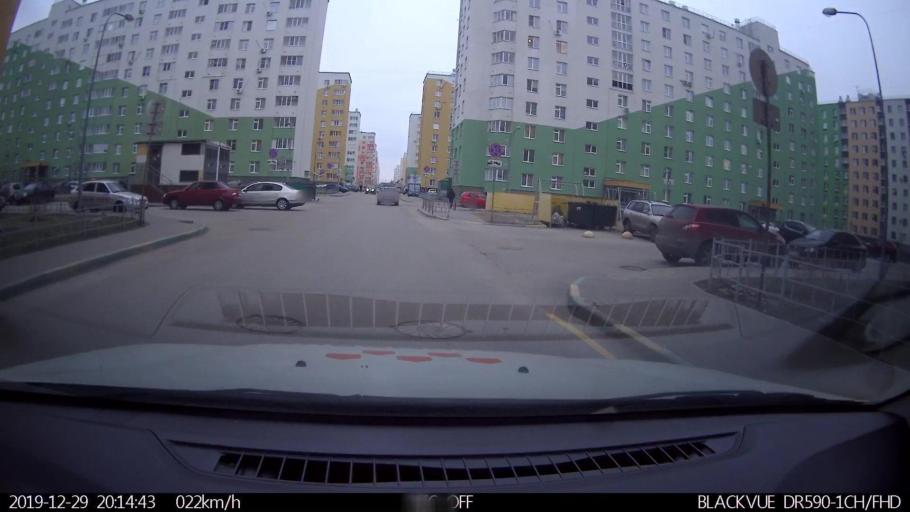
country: RU
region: Nizjnij Novgorod
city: Nizhniy Novgorod
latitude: 56.3410
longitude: 43.9172
